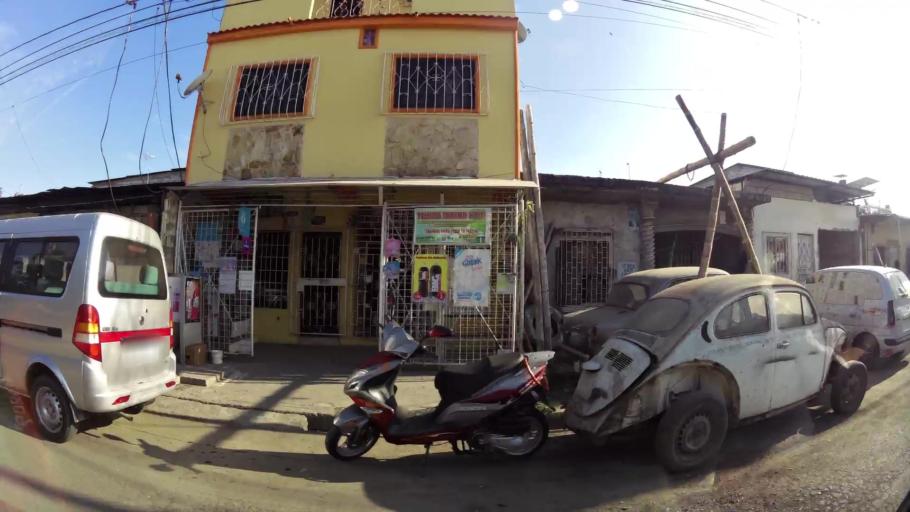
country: EC
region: Guayas
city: Guayaquil
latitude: -2.2221
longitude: -79.9178
